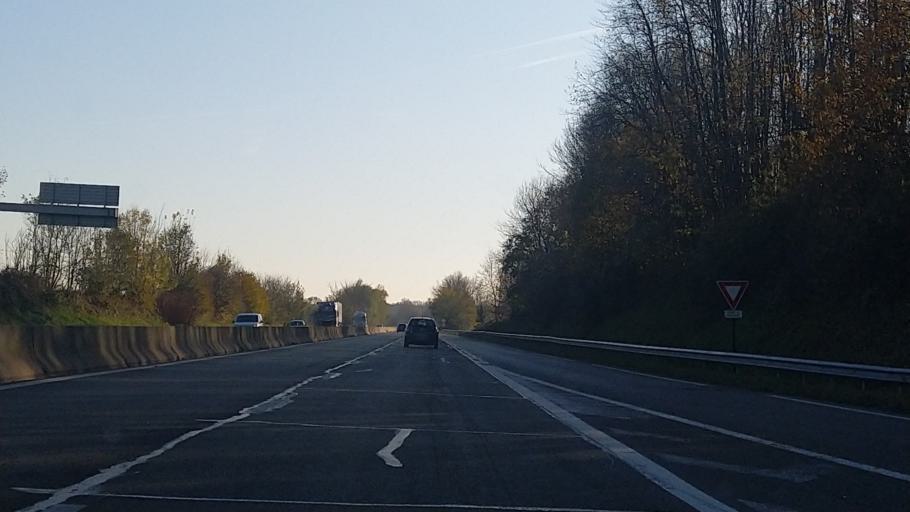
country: FR
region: Ile-de-France
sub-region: Departement du Val-d'Oise
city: Saint-Brice-sous-Foret
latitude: 49.0176
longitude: 2.3518
